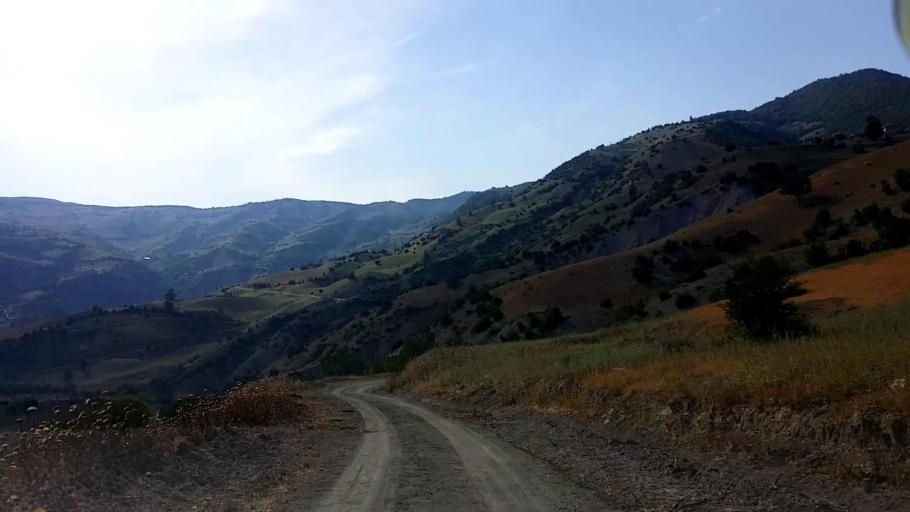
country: IR
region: Mazandaran
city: Chalus
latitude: 36.5463
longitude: 51.2962
